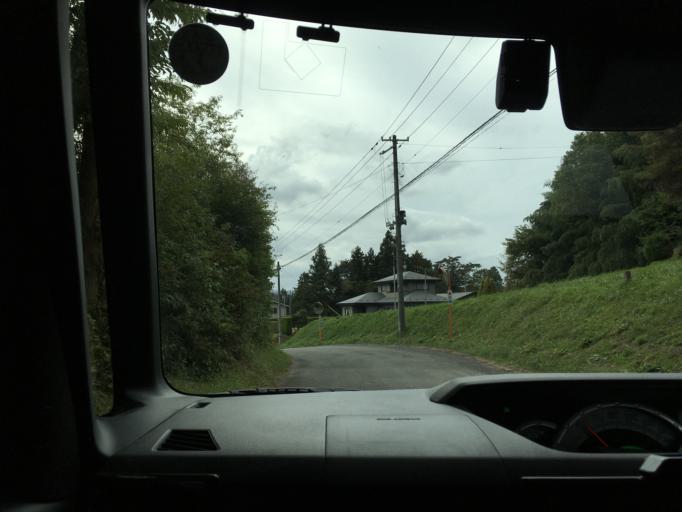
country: JP
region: Iwate
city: Ichinoseki
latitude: 39.0220
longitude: 141.3512
